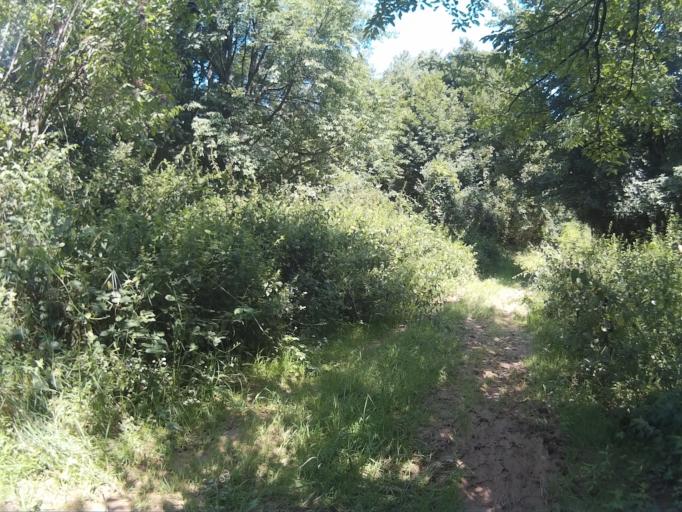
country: HU
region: Veszprem
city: Zirc
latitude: 47.1976
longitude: 17.8885
